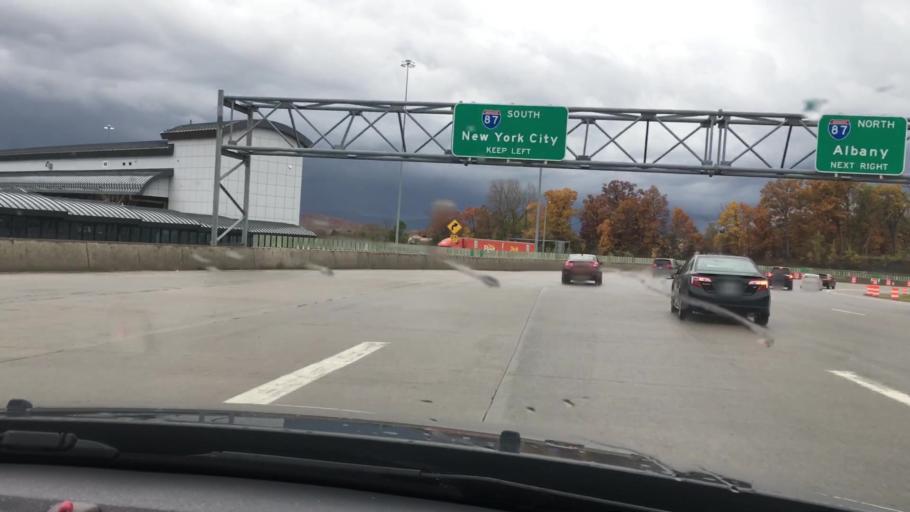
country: US
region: New York
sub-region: Orange County
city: Gardnertown
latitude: 41.5115
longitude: -74.0710
